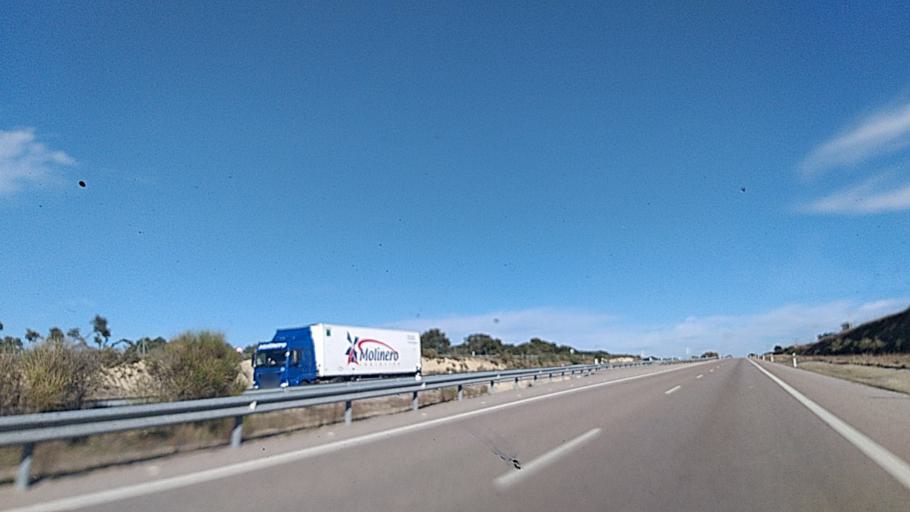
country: ES
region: Castille and Leon
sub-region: Provincia de Salamanca
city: Fuentes de Onoro
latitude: 40.5873
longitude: -6.7649
